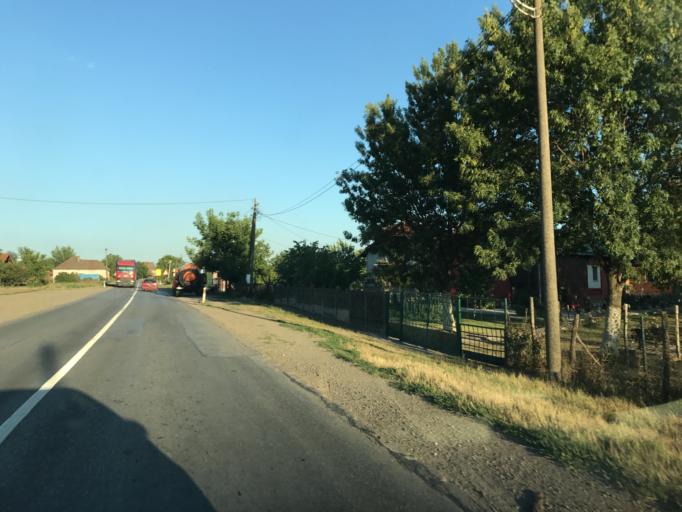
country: RS
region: Central Serbia
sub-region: Podunavski Okrug
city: Smederevo
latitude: 44.5966
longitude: 20.9674
